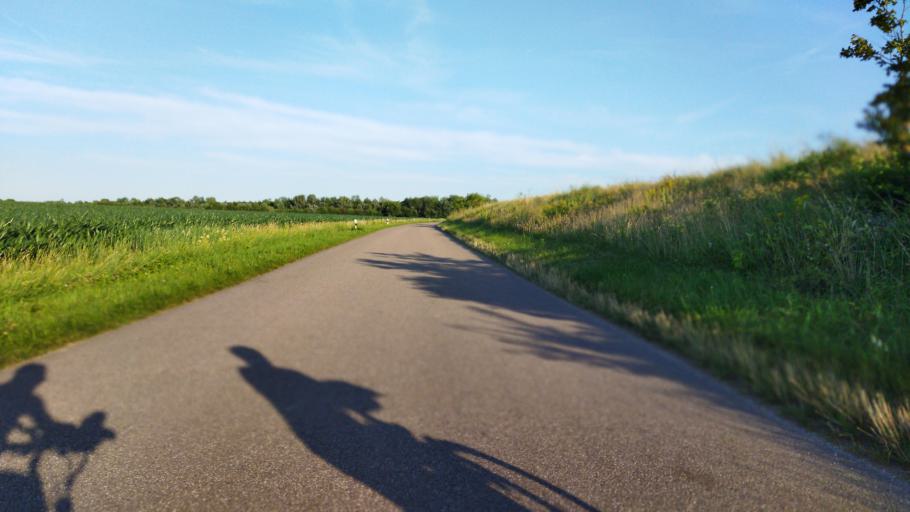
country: DE
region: Bavaria
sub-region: Upper Palatinate
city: Wiesent
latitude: 49.0023
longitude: 12.3420
